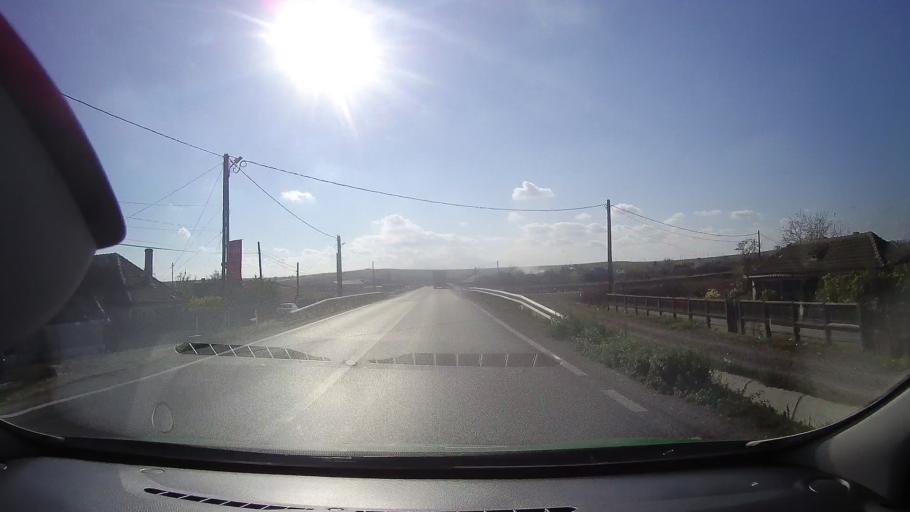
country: RO
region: Tulcea
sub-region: Comuna Baia
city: Baia
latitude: 44.7245
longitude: 28.6799
